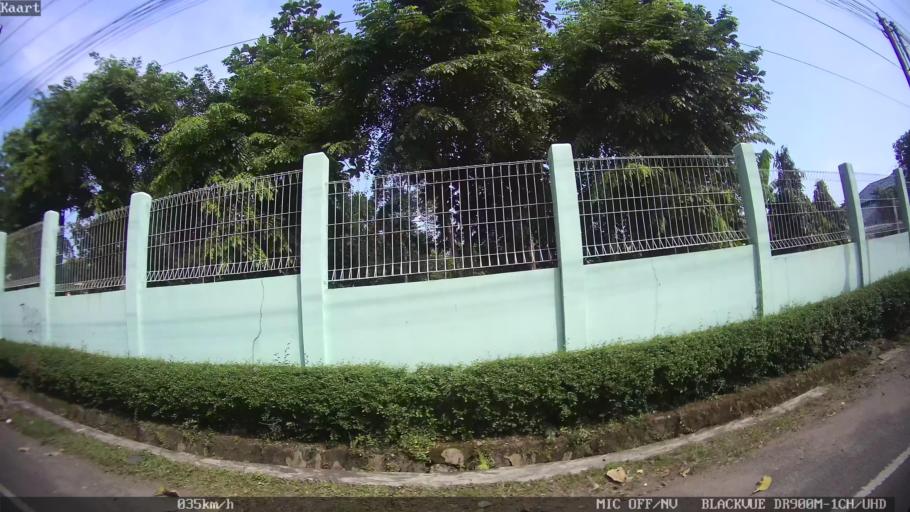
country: ID
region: Lampung
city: Kedaton
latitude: -5.3748
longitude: 105.2508
